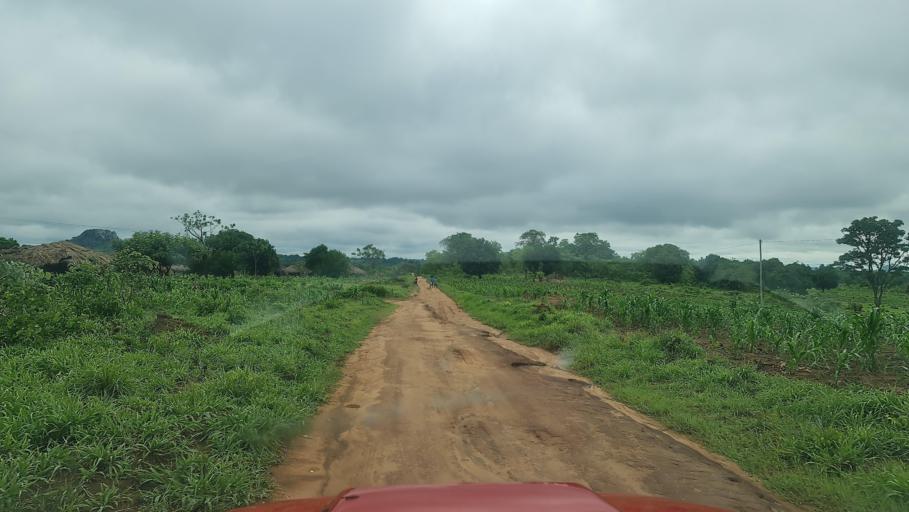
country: MW
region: Southern Region
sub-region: Nsanje District
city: Nsanje
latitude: -17.1930
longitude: 35.8603
